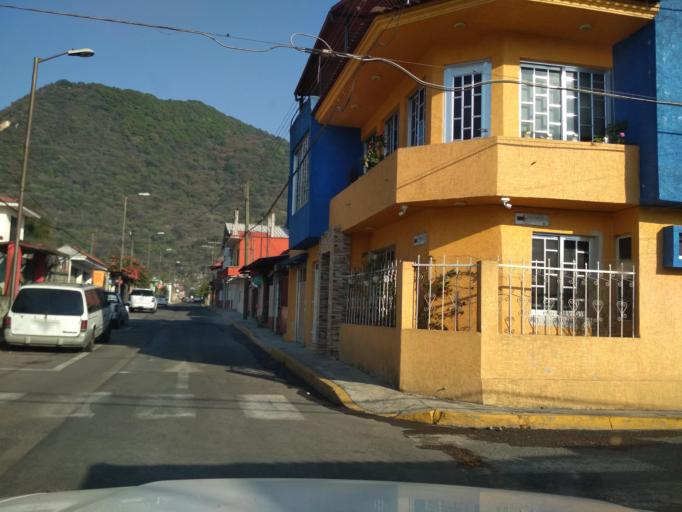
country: MX
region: Veracruz
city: Ixtac Zoquitlan
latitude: 18.8566
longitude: -97.0773
